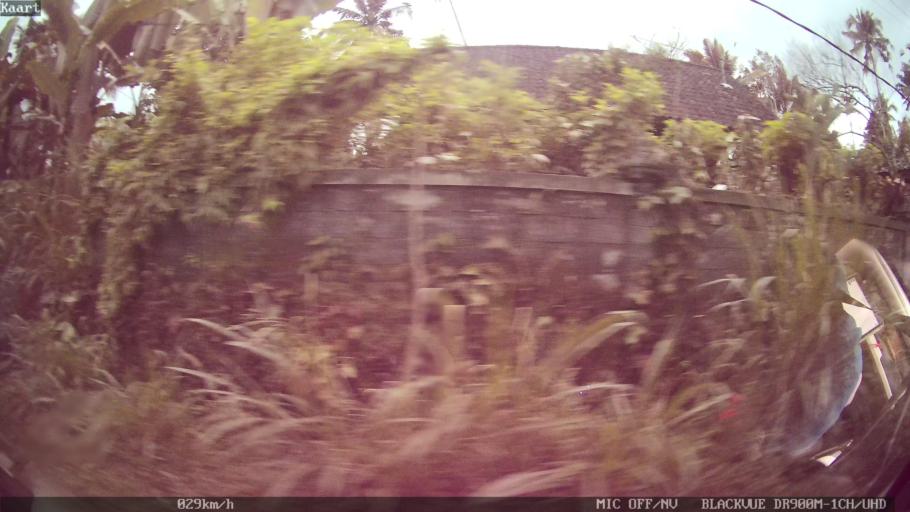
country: ID
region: Bali
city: Banjar Wangsian
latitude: -8.4500
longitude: 115.4210
